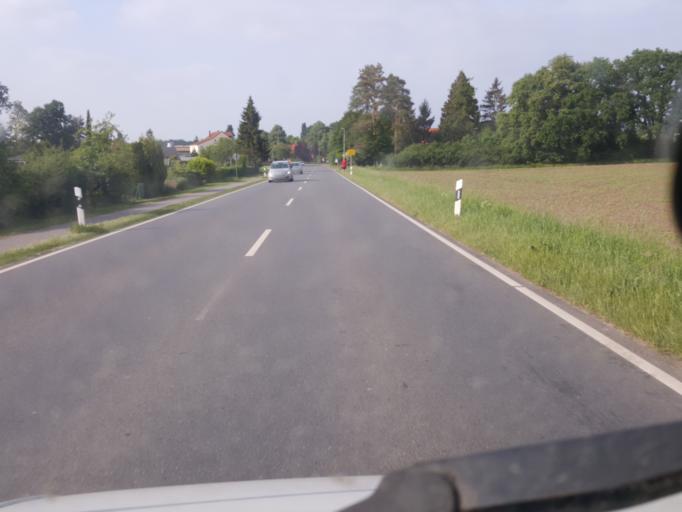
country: DE
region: Lower Saxony
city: Liebenau
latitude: 52.5967
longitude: 9.0985
